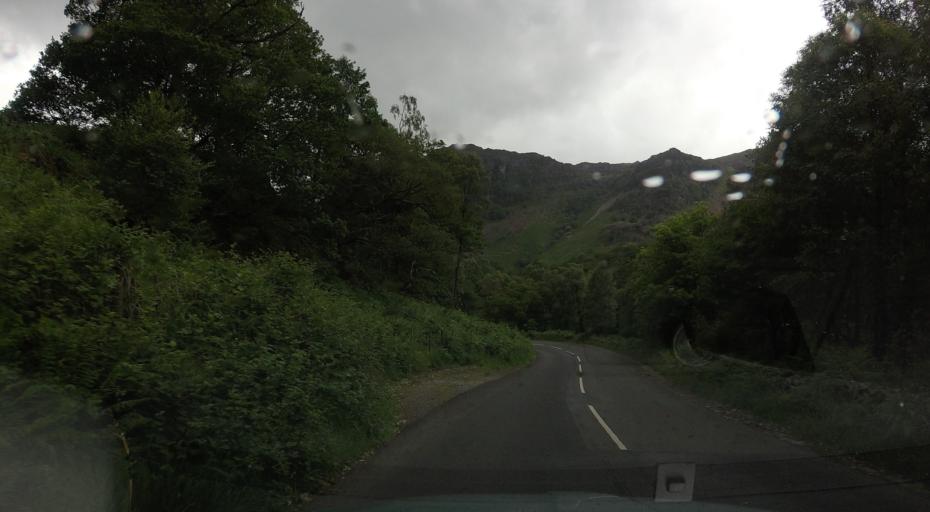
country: GB
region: England
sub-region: Cumbria
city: Keswick
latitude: 54.5430
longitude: -3.1552
